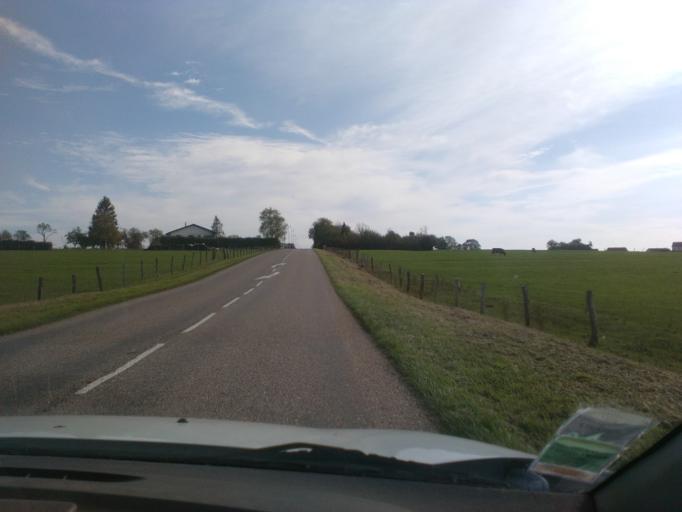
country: FR
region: Lorraine
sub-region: Departement des Vosges
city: Rambervillers
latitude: 48.3500
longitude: 6.5295
